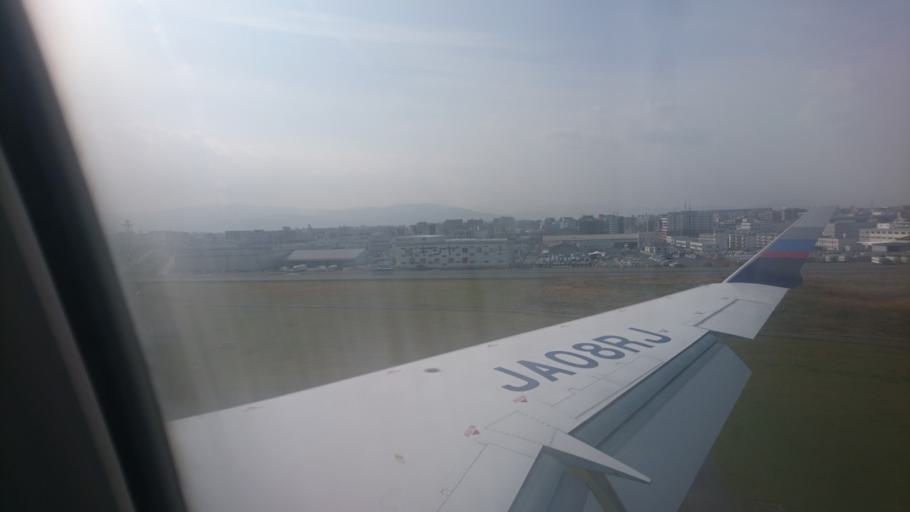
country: JP
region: Fukuoka
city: Fukuoka-shi
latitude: 33.5977
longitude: 130.4426
